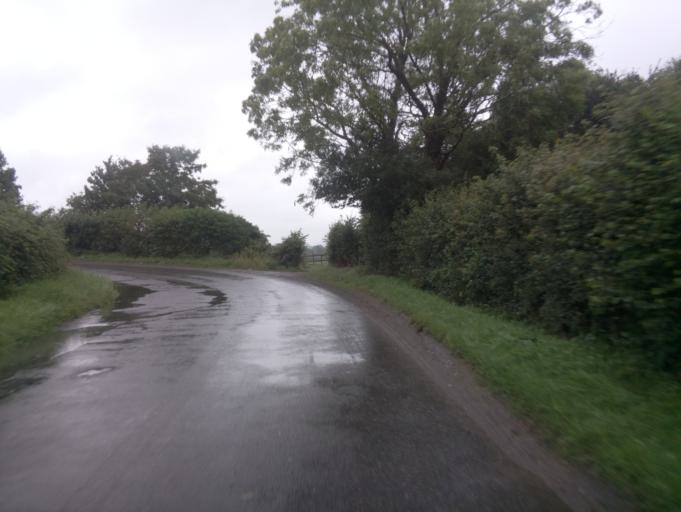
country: GB
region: England
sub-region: Gloucestershire
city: Uckington
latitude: 51.9312
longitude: -2.1150
